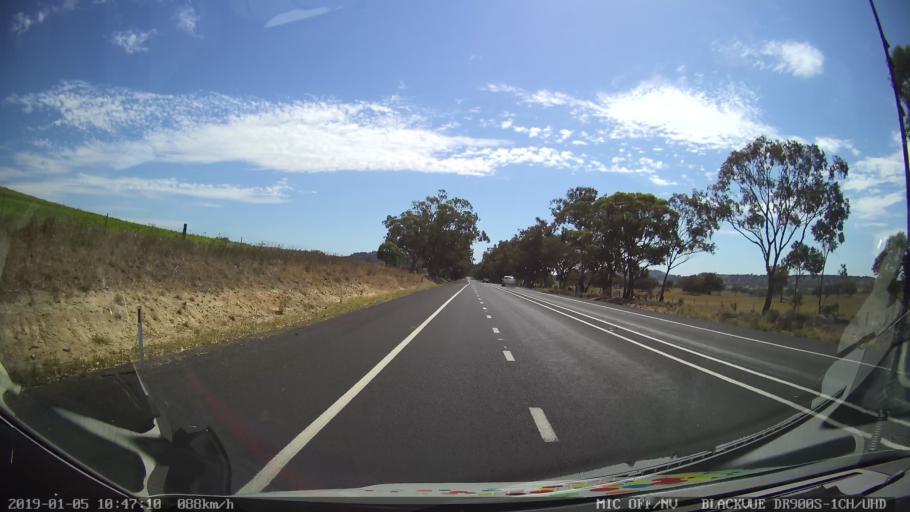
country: AU
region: New South Wales
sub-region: Warrumbungle Shire
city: Coonabarabran
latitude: -31.4471
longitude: 149.0295
